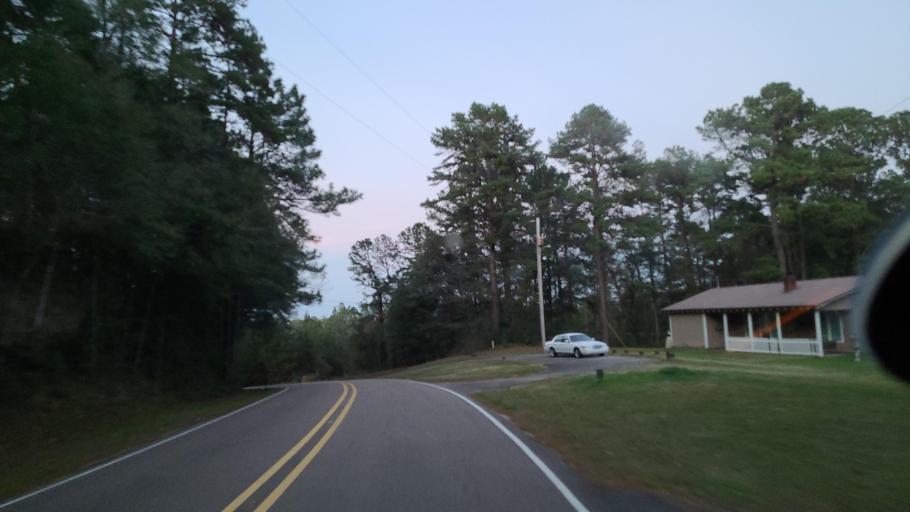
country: US
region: Mississippi
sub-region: Forrest County
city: Hattiesburg
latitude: 31.2408
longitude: -89.2418
